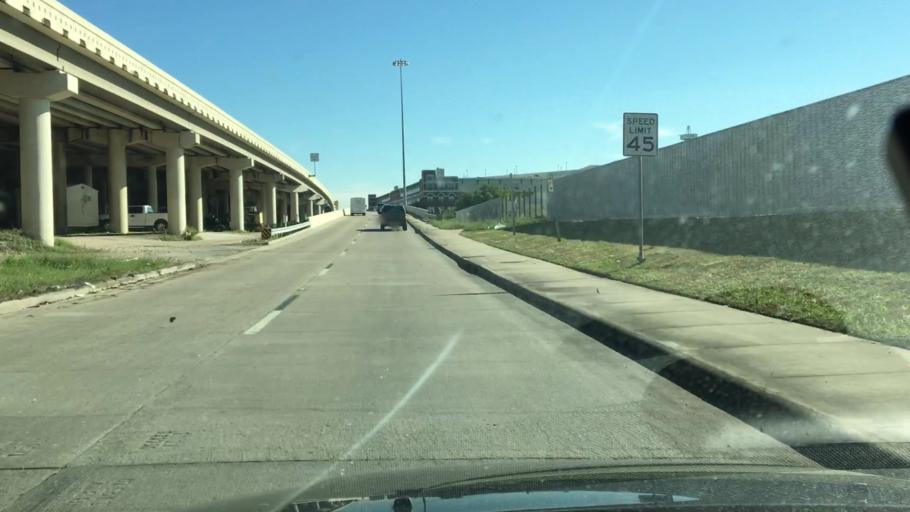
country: US
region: Texas
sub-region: Harris County
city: Houston
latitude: 29.7764
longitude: -95.3878
